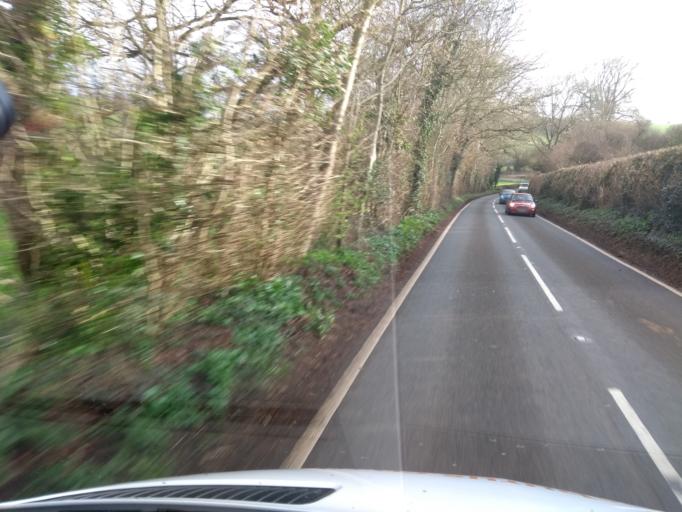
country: GB
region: England
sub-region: Somerset
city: Bruton
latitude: 51.0871
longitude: -2.4667
